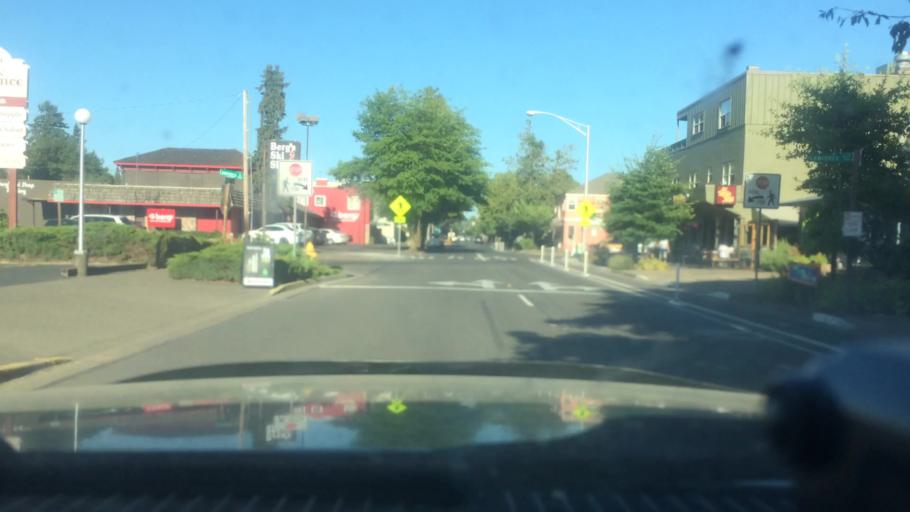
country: US
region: Oregon
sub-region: Lane County
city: Eugene
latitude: 44.0455
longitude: -123.0993
